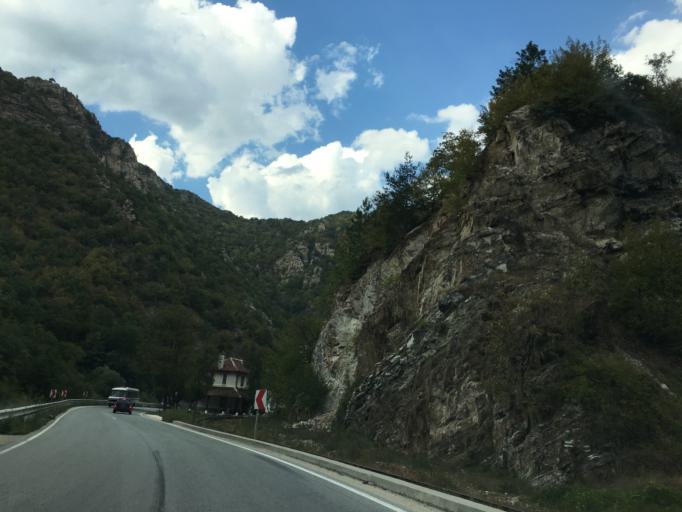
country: BG
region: Pazardzhik
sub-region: Obshtina Septemvri
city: Septemvri
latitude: 42.1060
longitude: 24.1059
